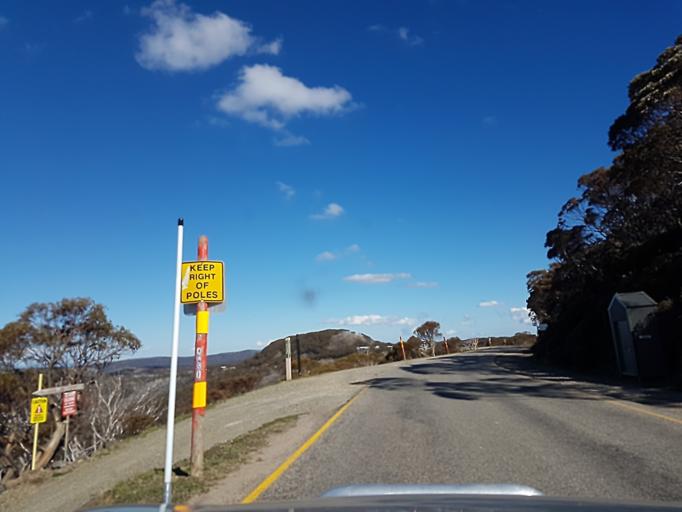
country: AU
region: Victoria
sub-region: Alpine
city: Mount Beauty
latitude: -36.9854
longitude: 147.1470
